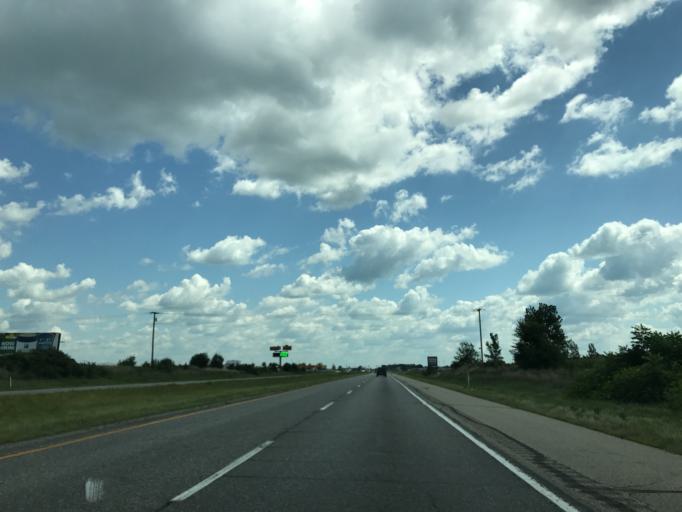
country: US
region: Indiana
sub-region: Marshall County
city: Plymouth
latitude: 41.3612
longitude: -86.3571
